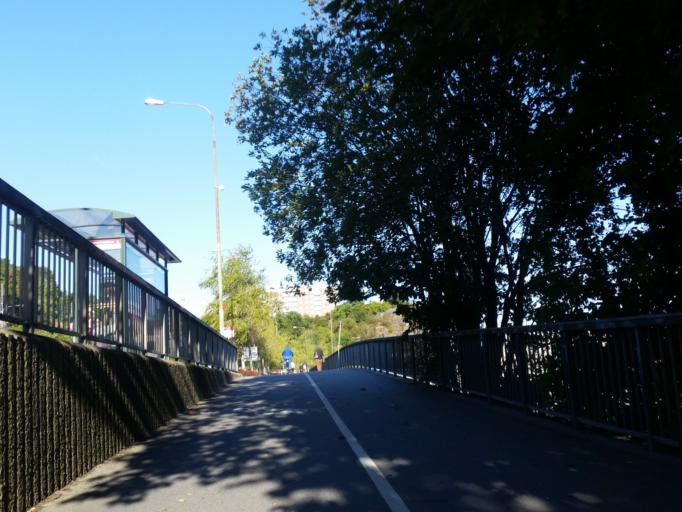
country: SE
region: Stockholm
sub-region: Stockholms Kommun
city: OEstermalm
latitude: 59.3146
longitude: 18.0983
